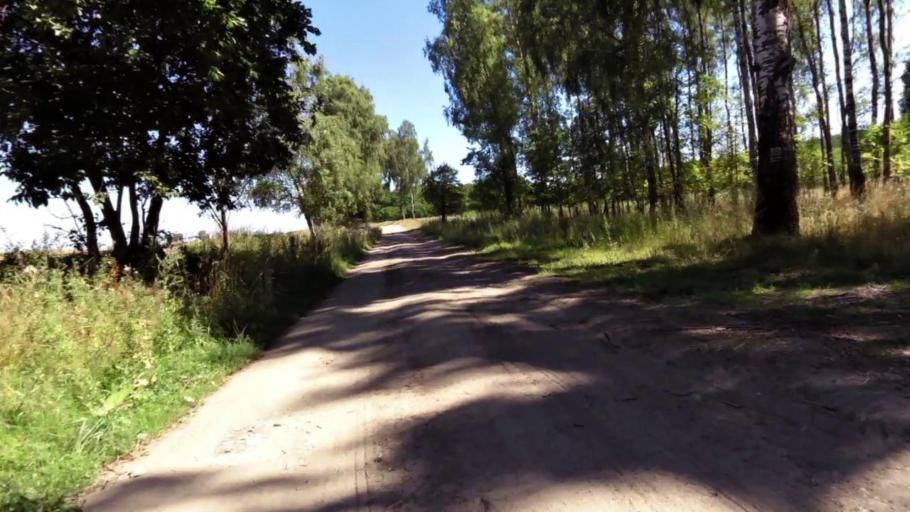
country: PL
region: West Pomeranian Voivodeship
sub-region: Powiat szczecinecki
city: Szczecinek
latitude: 53.6288
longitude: 16.6610
